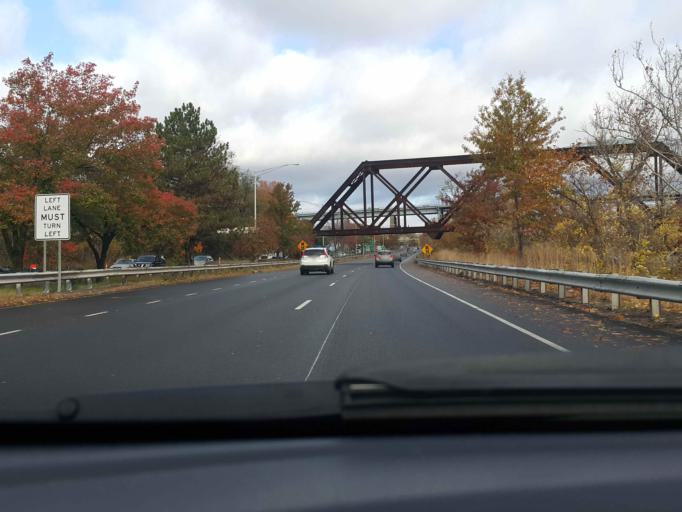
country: US
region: Connecticut
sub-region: Middlesex County
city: Middletown
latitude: 41.5654
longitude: -72.6492
